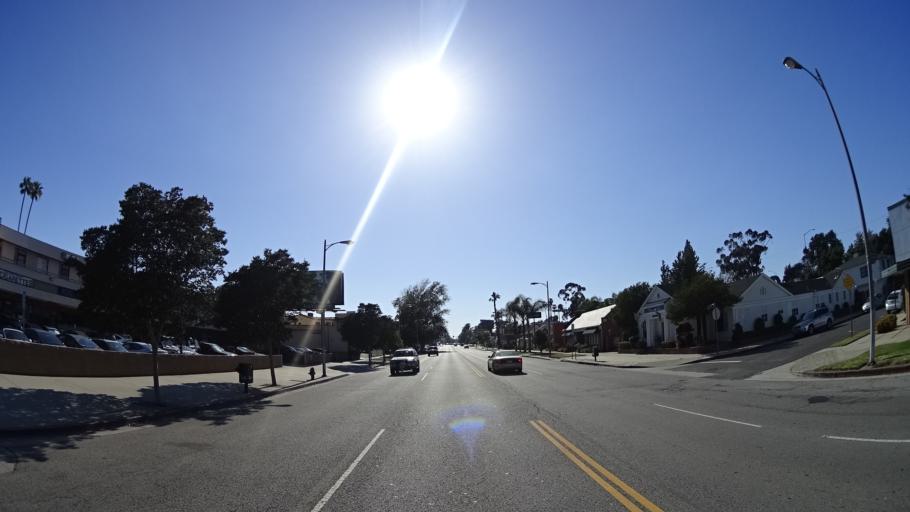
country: US
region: California
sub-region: Los Angeles County
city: Universal City
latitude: 34.1523
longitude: -118.3637
